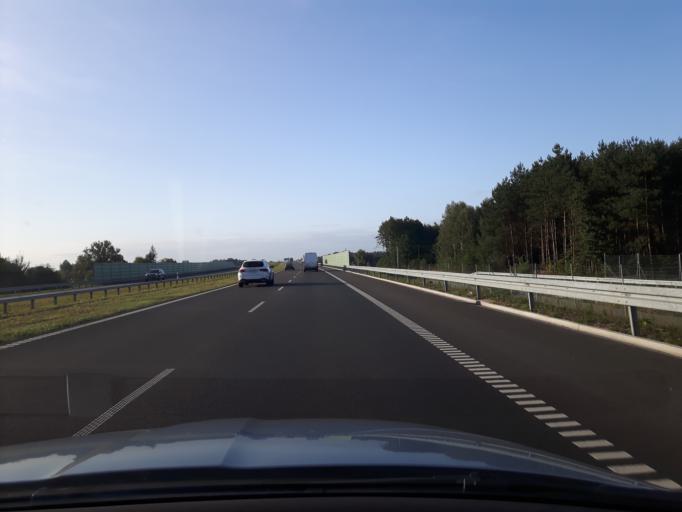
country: PL
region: Masovian Voivodeship
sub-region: Powiat radomski
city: Wolanow
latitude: 51.3594
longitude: 21.0134
